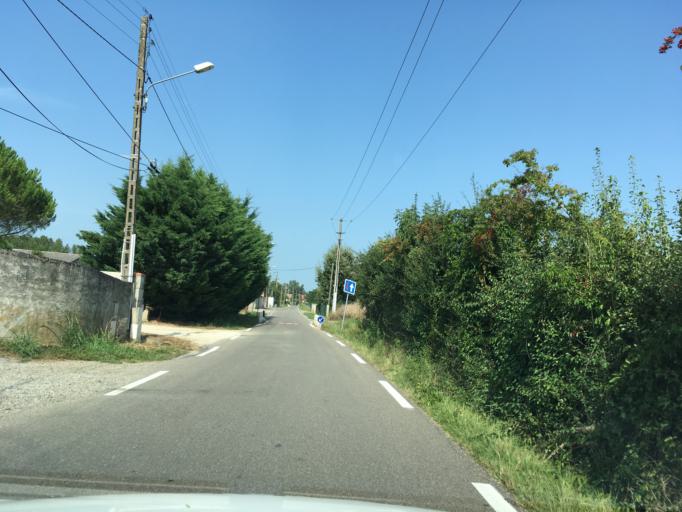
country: FR
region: Midi-Pyrenees
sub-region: Departement du Tarn-et-Garonne
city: Montauban
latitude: 44.0110
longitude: 1.3372
